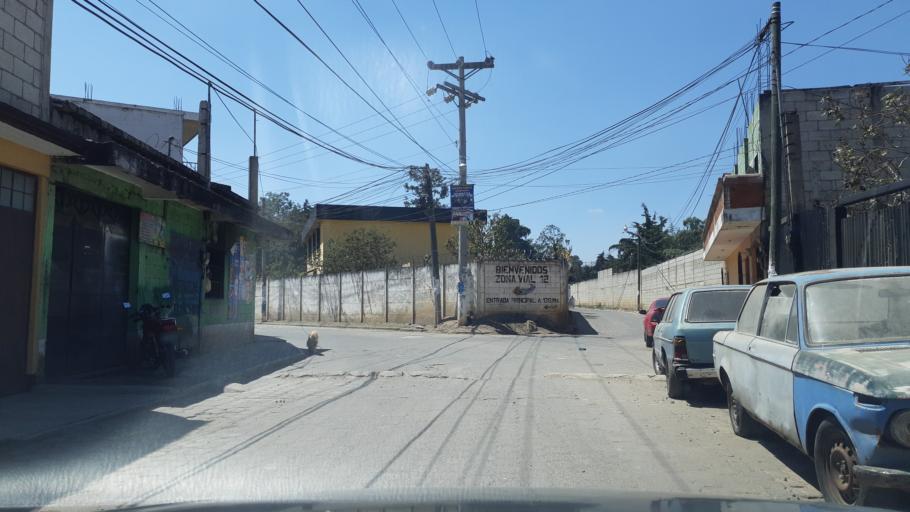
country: GT
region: Chimaltenango
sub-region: Municipio de Chimaltenango
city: Chimaltenango
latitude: 14.6535
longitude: -90.8114
